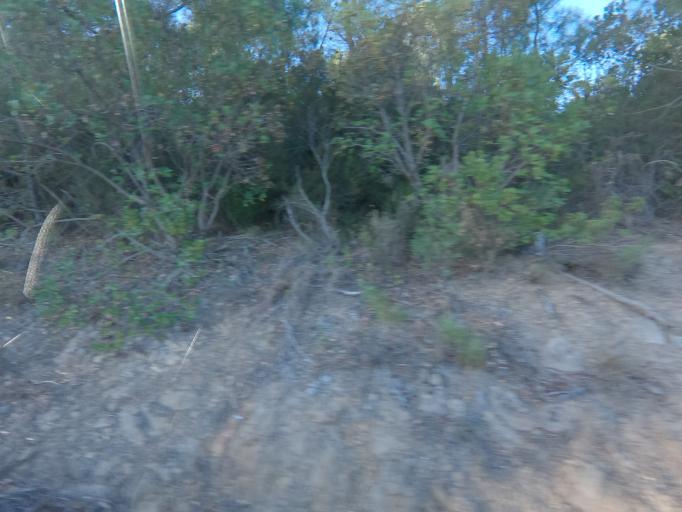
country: PT
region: Vila Real
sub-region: Sabrosa
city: Sabrosa
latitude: 41.2632
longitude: -7.5629
